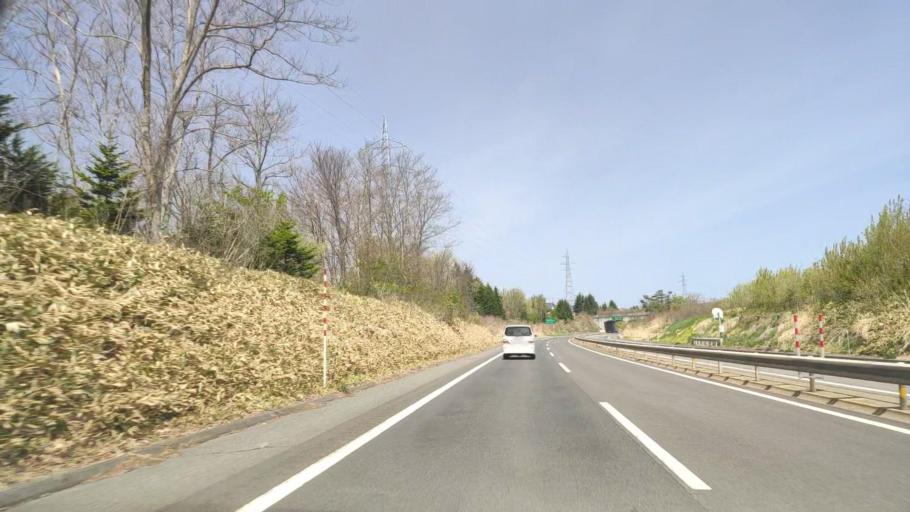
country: JP
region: Aomori
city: Hachinohe
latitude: 40.4751
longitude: 141.4602
